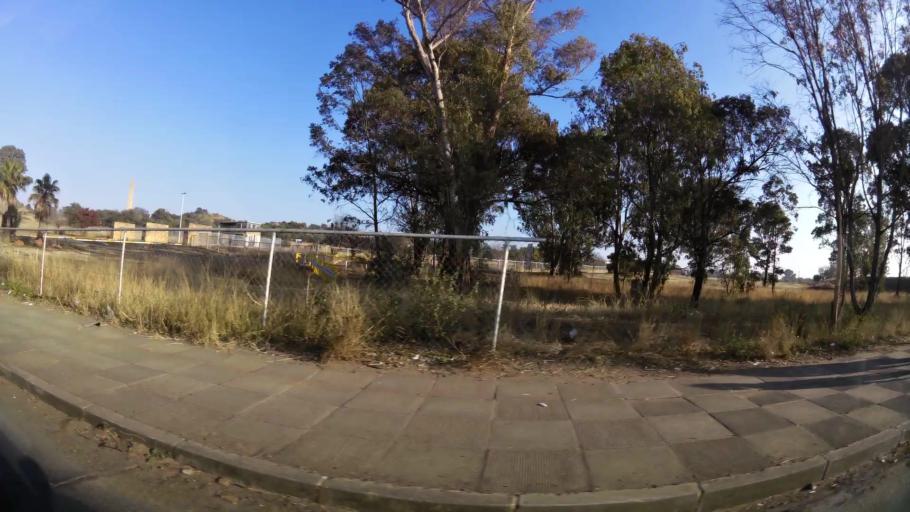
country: ZA
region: Orange Free State
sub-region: Mangaung Metropolitan Municipality
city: Bloemfontein
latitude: -29.1411
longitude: 26.2117
